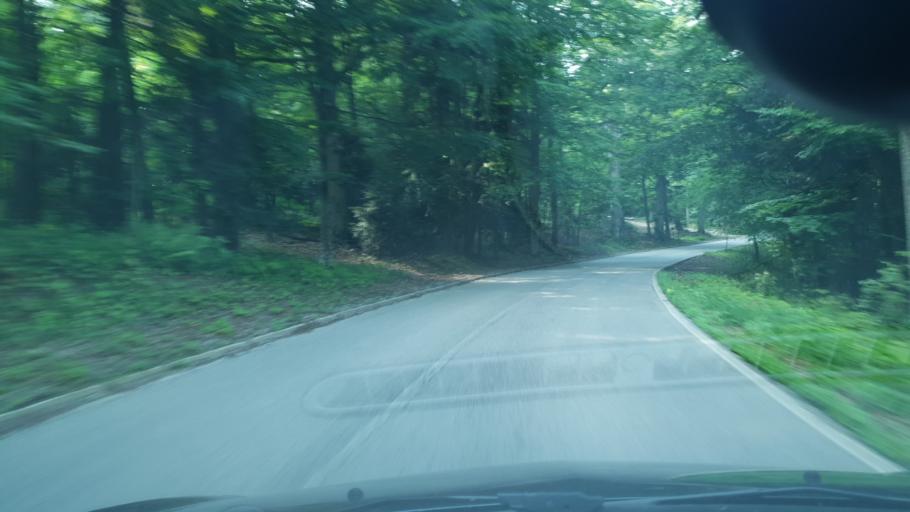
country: HR
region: Grad Zagreb
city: Kasina
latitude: 45.9101
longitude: 15.9735
